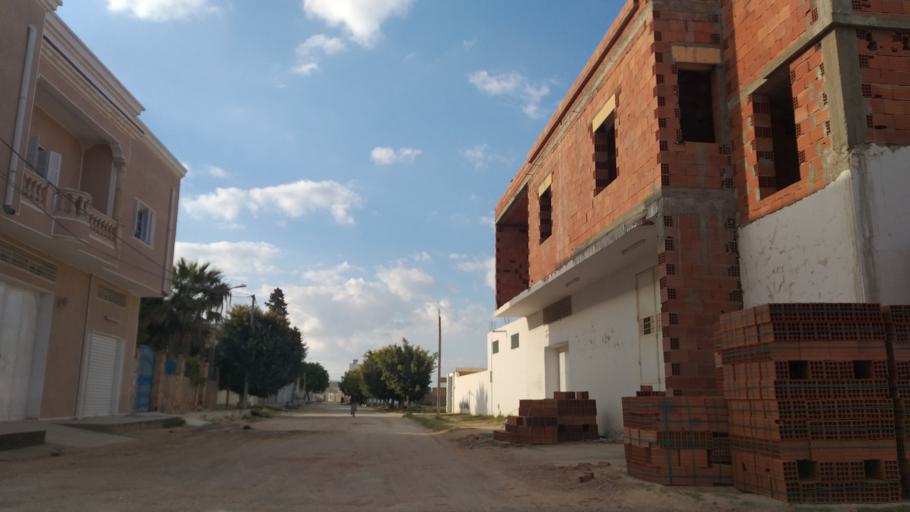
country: TN
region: Al Mahdiyah
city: El Jem
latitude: 35.3035
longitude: 10.7023
